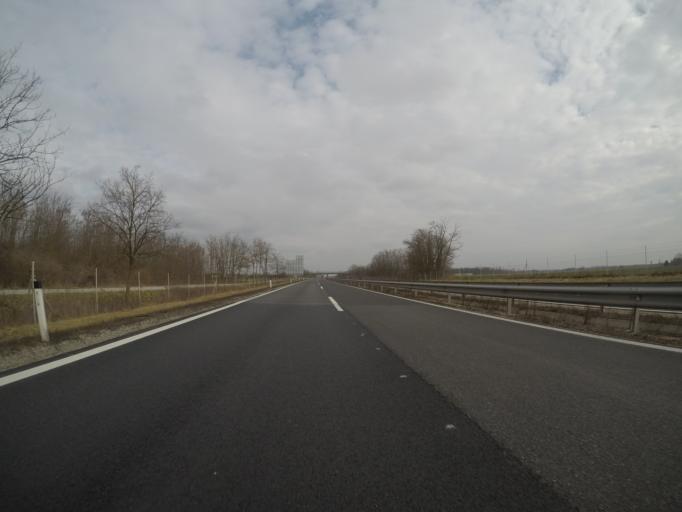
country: SI
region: Murska Sobota
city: Murska Sobota
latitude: 46.6355
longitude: 16.1775
